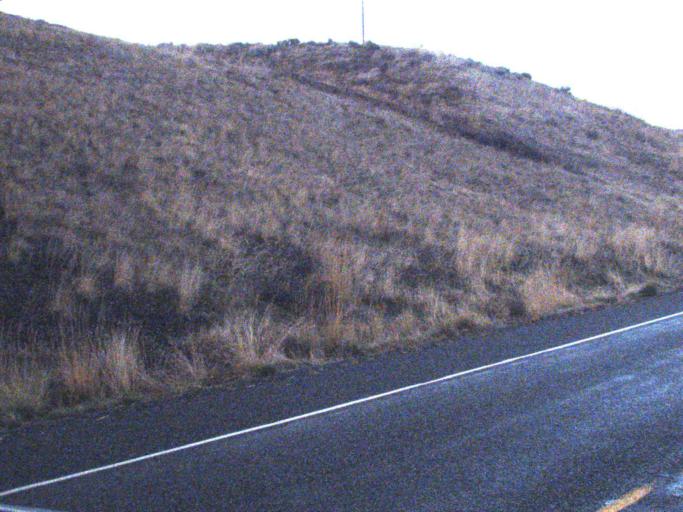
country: US
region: Washington
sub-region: Garfield County
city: Pomeroy
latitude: 46.6110
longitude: -117.7893
